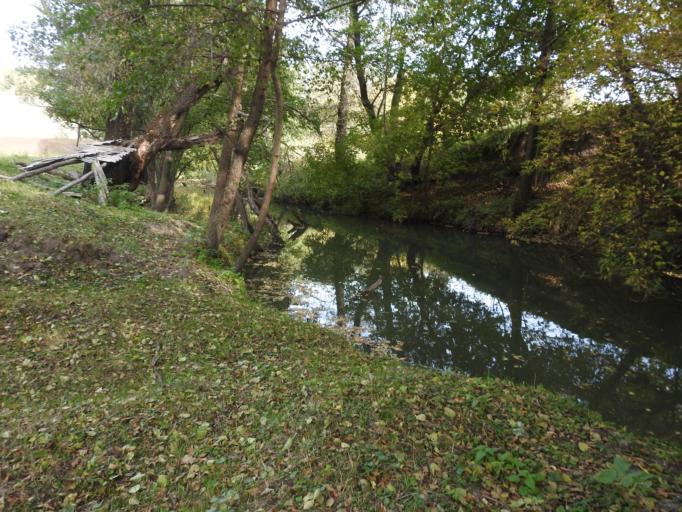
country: RU
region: Saratov
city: Baltay
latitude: 52.5400
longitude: 46.6523
